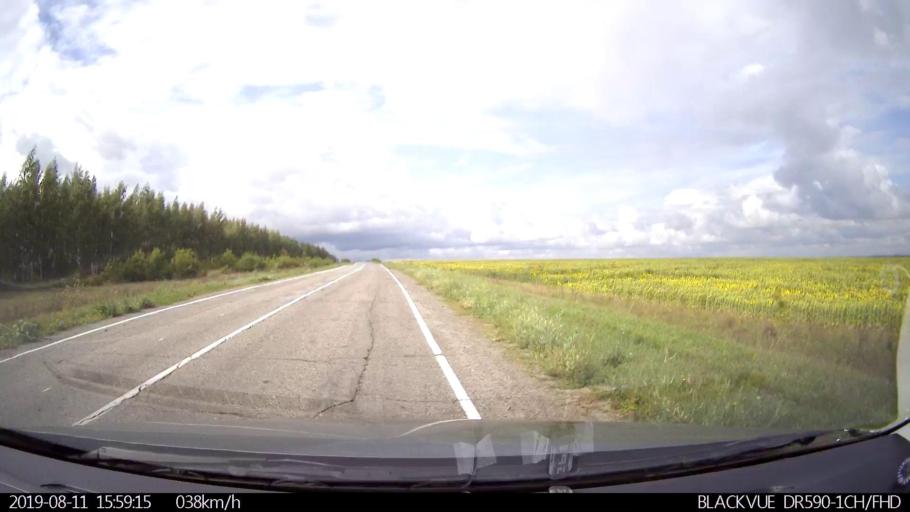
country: RU
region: Ulyanovsk
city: Ignatovka
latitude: 53.9600
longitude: 47.6490
